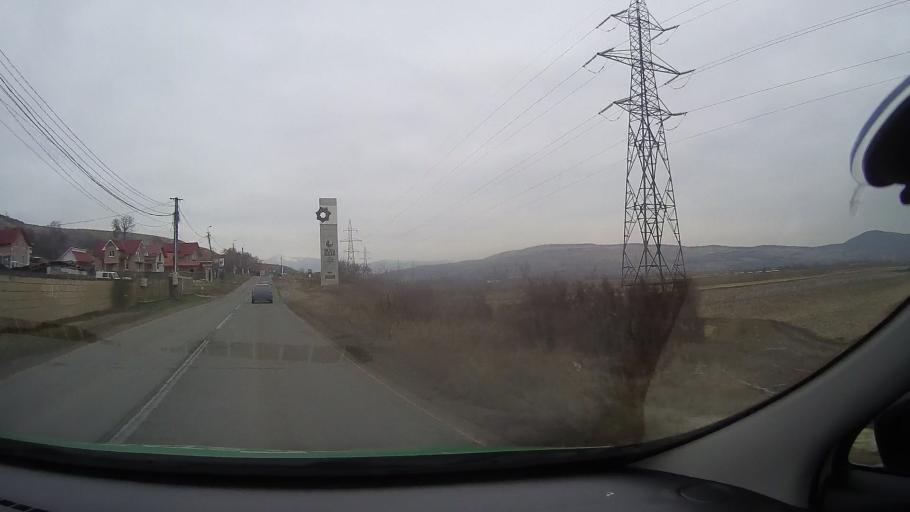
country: RO
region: Alba
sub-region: Comuna Ighiu
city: Sard
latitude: 46.1135
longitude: 23.5388
